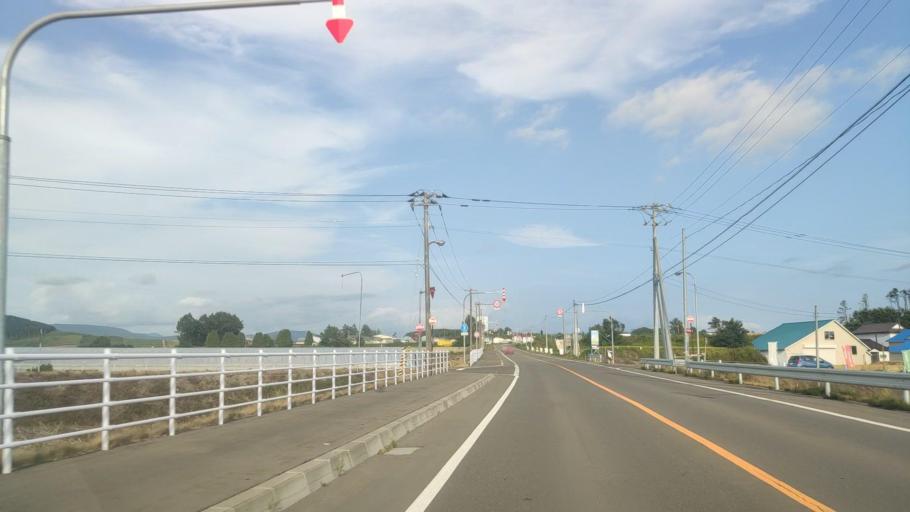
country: JP
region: Hokkaido
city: Iwamizawa
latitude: 43.0270
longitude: 141.8343
